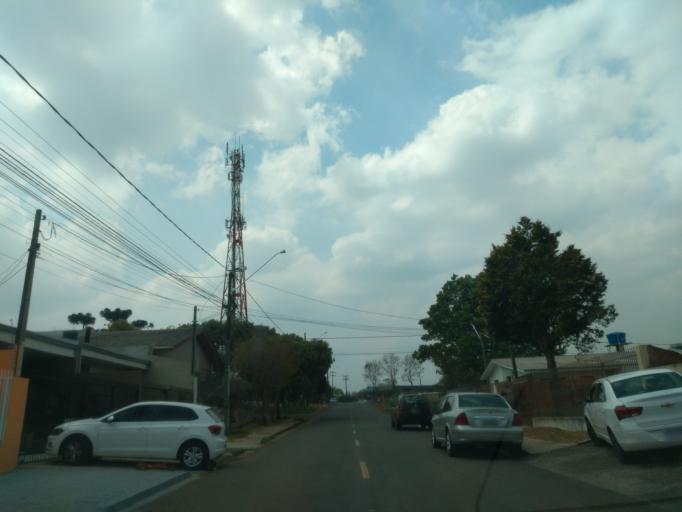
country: BR
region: Parana
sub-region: Guarapuava
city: Guarapuava
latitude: -25.3795
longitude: -51.4803
